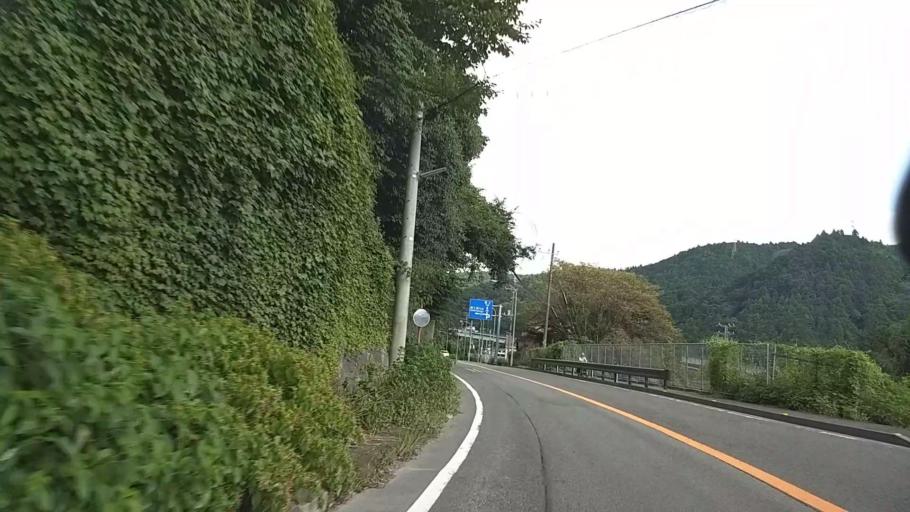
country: JP
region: Shizuoka
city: Fujinomiya
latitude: 35.1945
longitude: 138.5658
